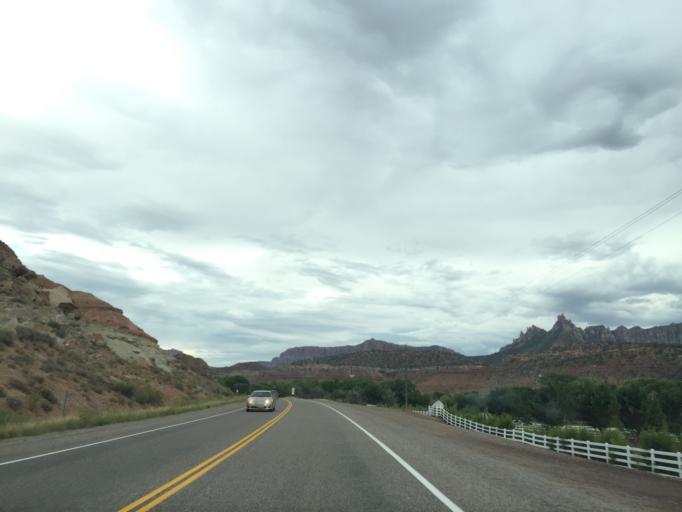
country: US
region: Utah
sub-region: Washington County
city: Hildale
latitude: 37.1618
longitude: -113.0560
